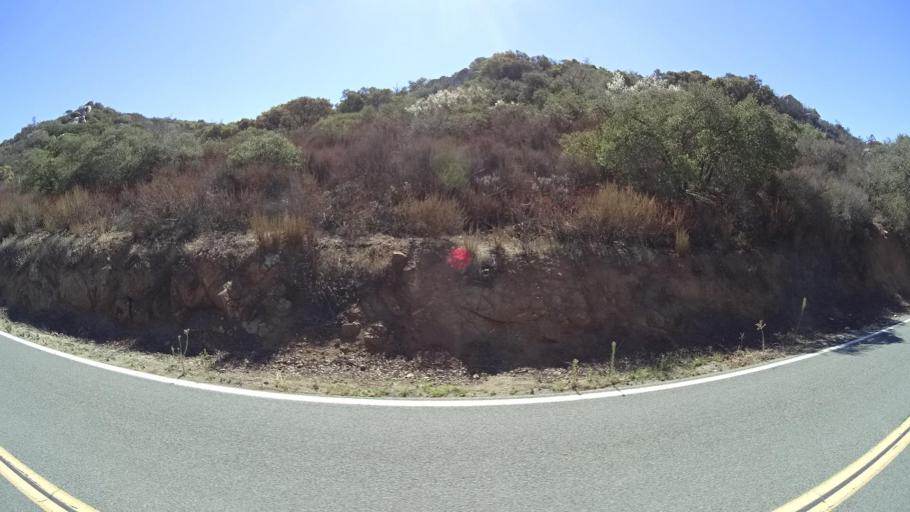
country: US
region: California
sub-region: San Diego County
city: Descanso
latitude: 32.7587
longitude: -116.6746
